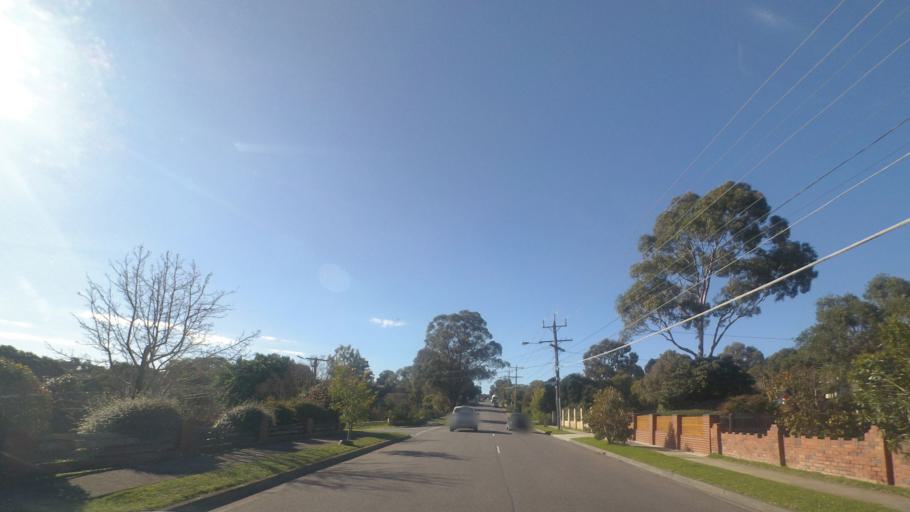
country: AU
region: Victoria
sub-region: Banyule
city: Montmorency
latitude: -37.7184
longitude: 145.1180
